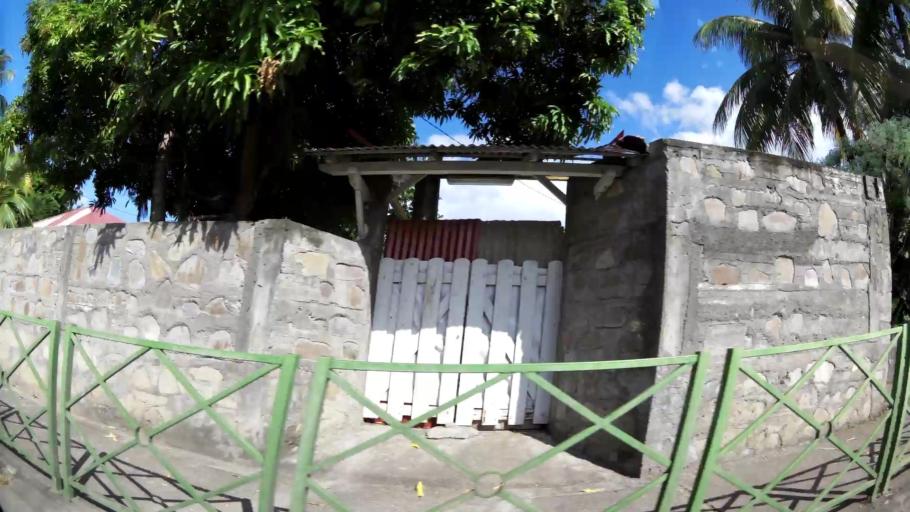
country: GP
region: Guadeloupe
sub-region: Guadeloupe
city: Vieux-Habitants
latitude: 16.0785
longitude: -61.7622
